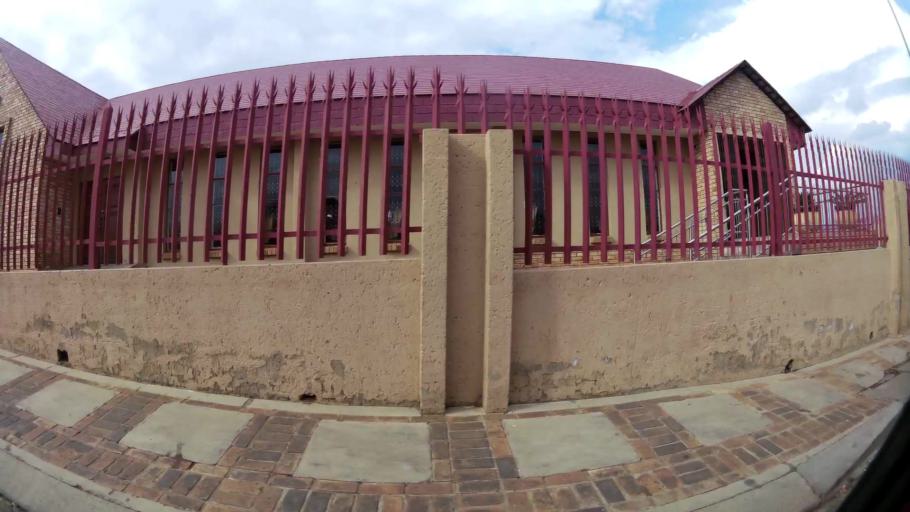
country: ZA
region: Gauteng
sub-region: City of Johannesburg Metropolitan Municipality
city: Soweto
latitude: -26.2362
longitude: 27.8694
